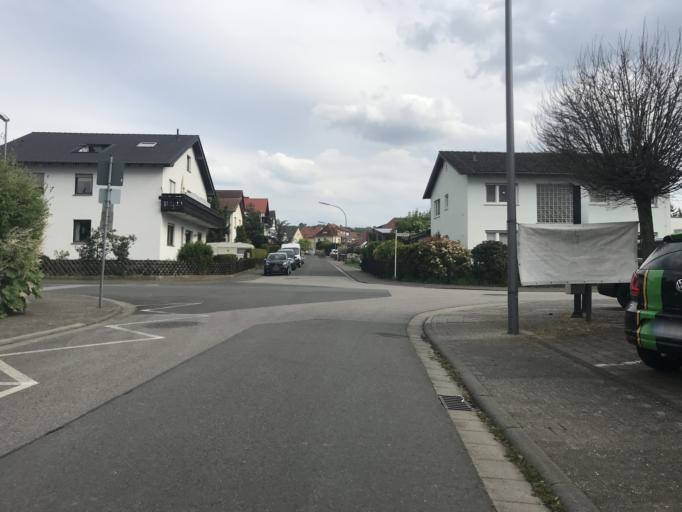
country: DE
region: Rheinland-Pfalz
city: Nieder-Ingelheim
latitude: 49.9846
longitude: 8.0685
